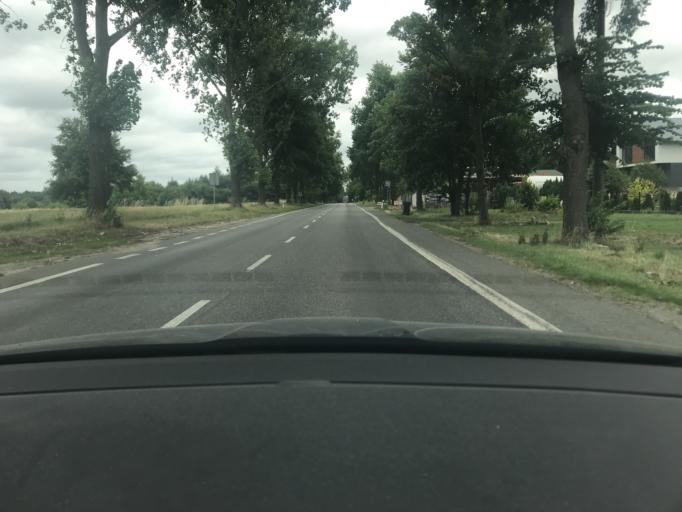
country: PL
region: Lodz Voivodeship
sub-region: Powiat poddebicki
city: Poddebice
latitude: 51.8909
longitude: 18.9736
